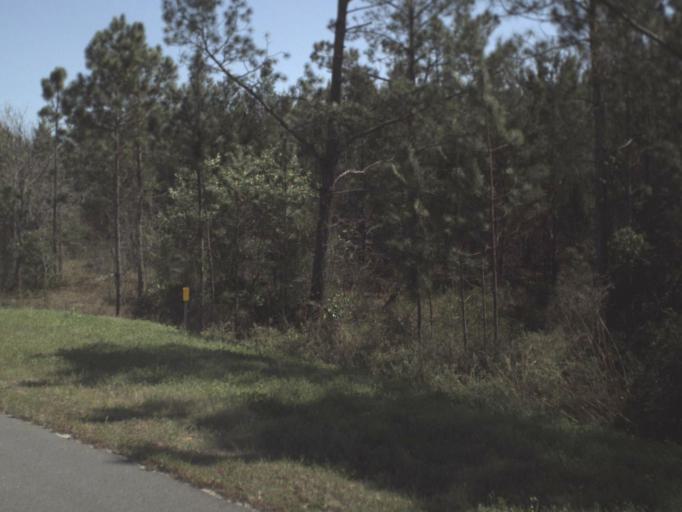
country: US
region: Florida
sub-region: Bay County
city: Youngstown
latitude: 30.4340
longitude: -85.2730
